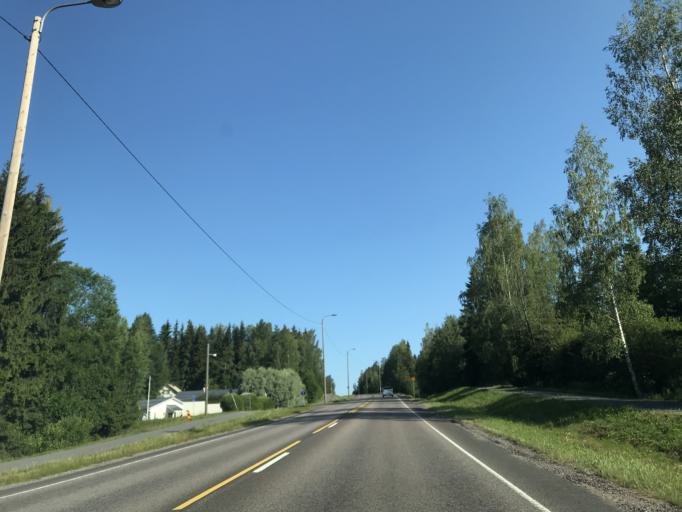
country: FI
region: Paijanne Tavastia
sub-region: Lahti
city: Lahti
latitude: 61.0309
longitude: 25.6735
